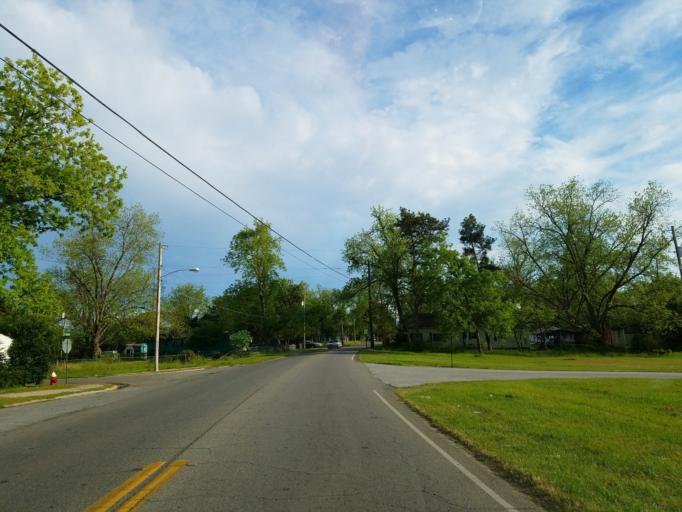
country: US
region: Georgia
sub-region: Crisp County
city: Cordele
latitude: 31.9776
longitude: -83.7883
